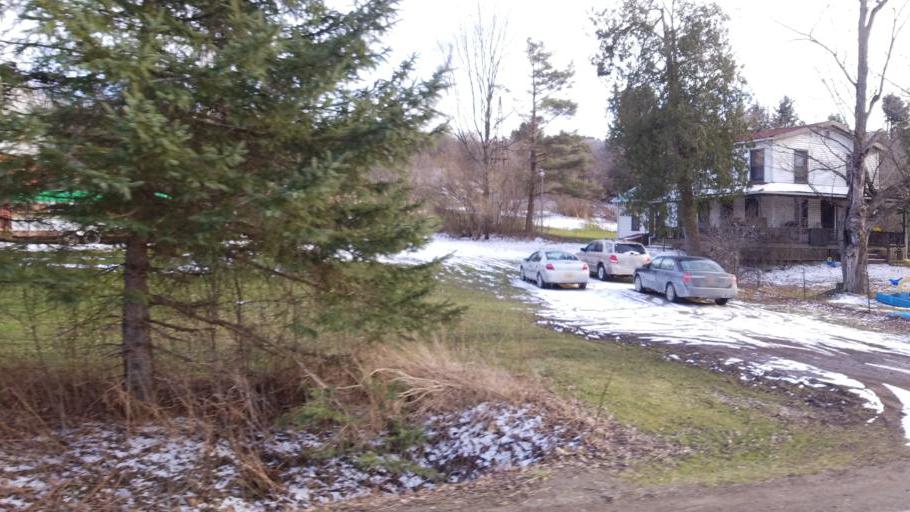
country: US
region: New York
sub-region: Allegany County
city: Wellsville
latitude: 42.1709
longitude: -77.9459
